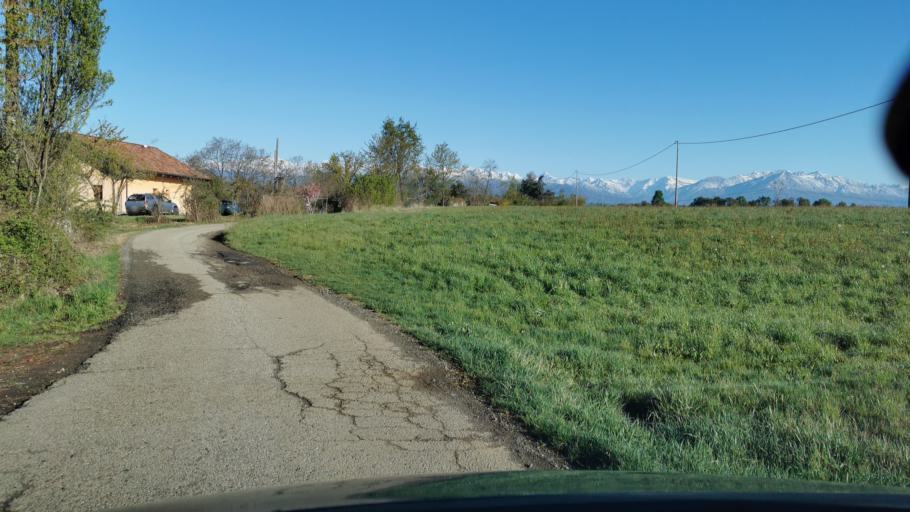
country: IT
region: Piedmont
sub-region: Provincia di Torino
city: Rivarossa
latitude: 45.2184
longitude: 7.7068
